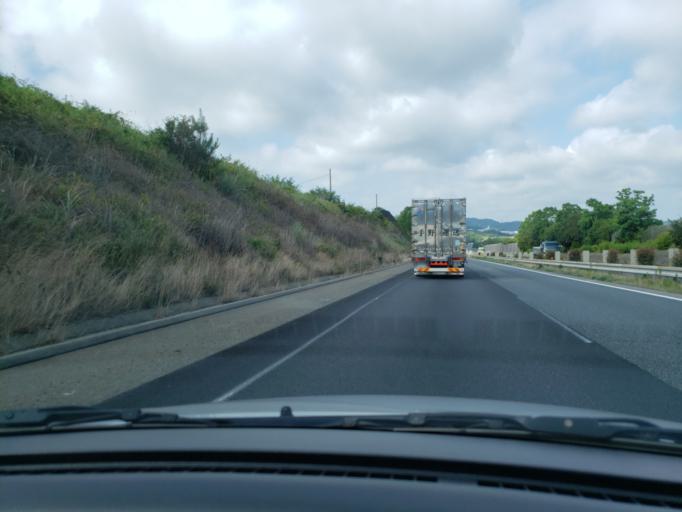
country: JP
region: Hiroshima
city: Onomichi
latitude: 34.4692
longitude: 133.2517
